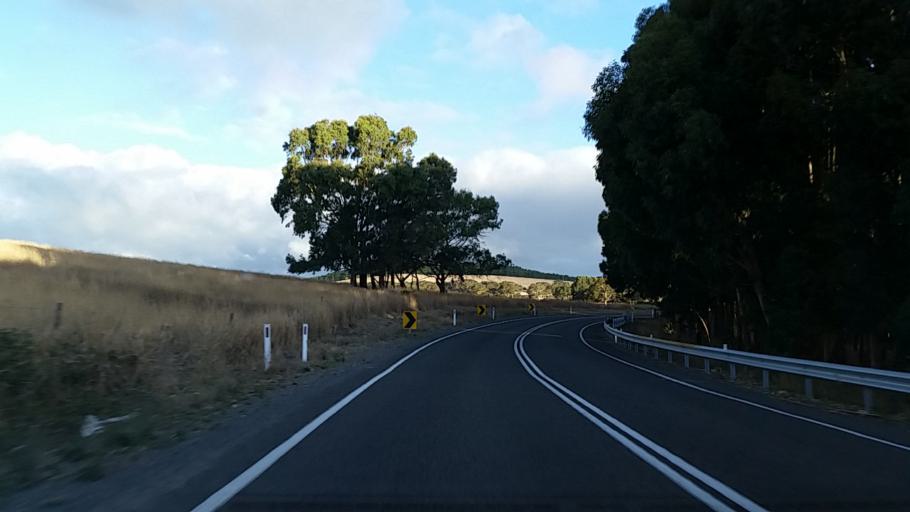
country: AU
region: South Australia
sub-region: Yankalilla
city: Normanville
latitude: -35.5611
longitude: 138.2001
